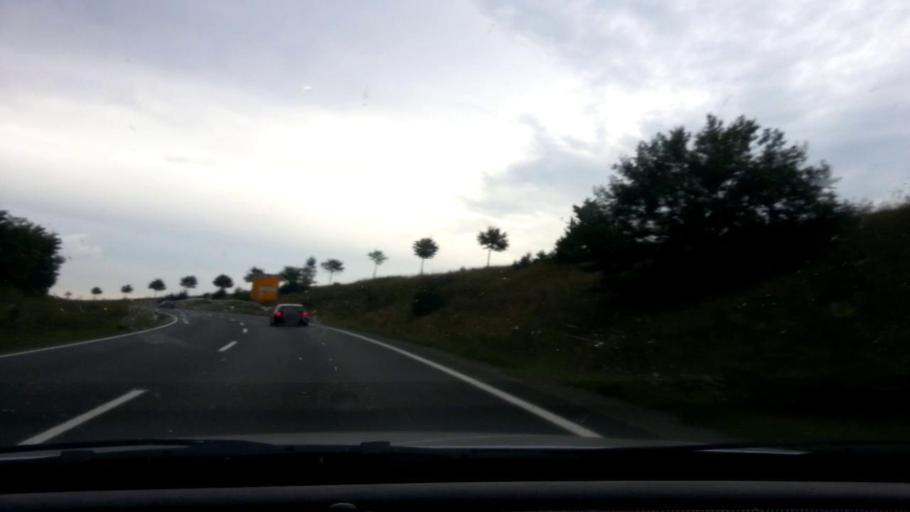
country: DE
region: Bavaria
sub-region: Upper Franconia
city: Neunkirchen am Main
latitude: 49.9245
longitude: 11.6351
